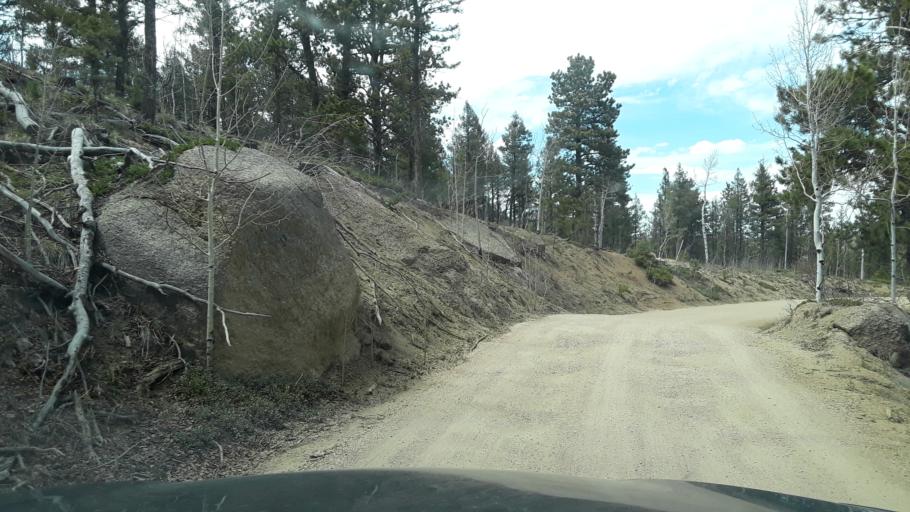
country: US
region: Colorado
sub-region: El Paso County
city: Palmer Lake
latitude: 39.0585
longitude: -104.9760
